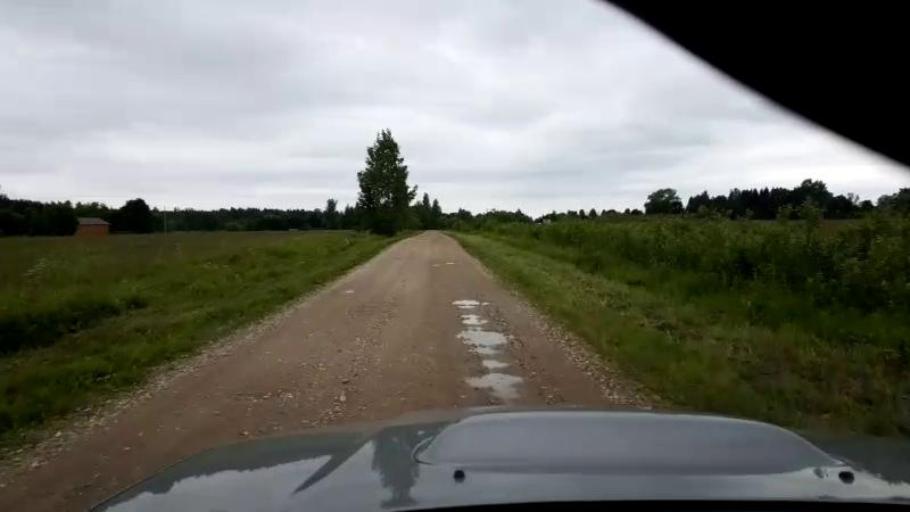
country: EE
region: Paernumaa
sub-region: Halinga vald
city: Parnu-Jaagupi
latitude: 58.5323
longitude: 24.5604
